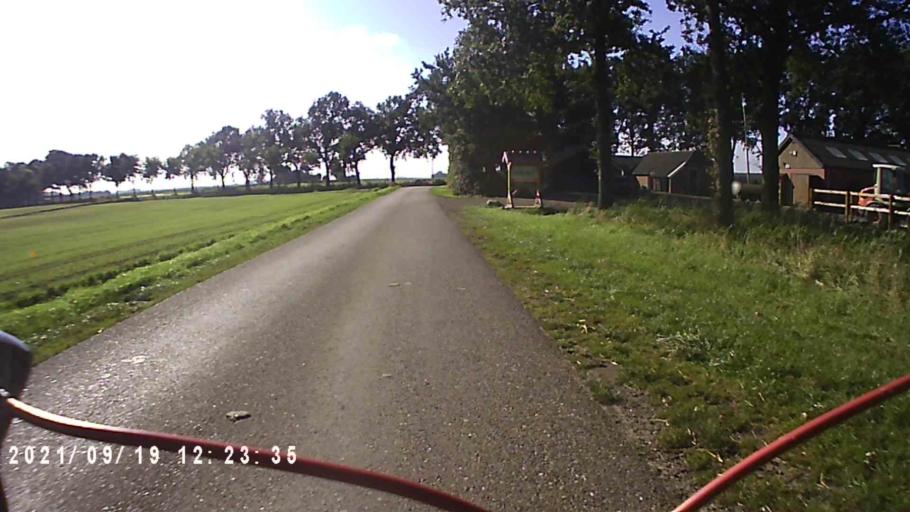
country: NL
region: Groningen
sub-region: Gemeente Appingedam
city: Appingedam
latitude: 53.2431
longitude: 6.8905
